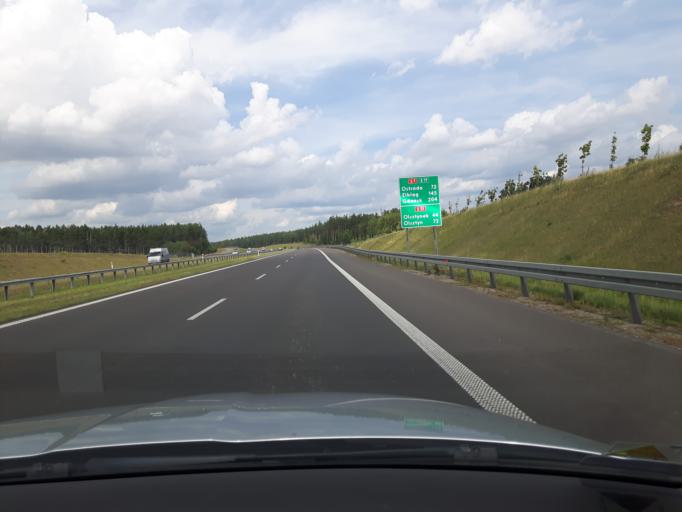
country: PL
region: Masovian Voivodeship
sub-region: Powiat mlawski
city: Wieczfnia Koscielna
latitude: 53.2352
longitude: 20.4216
